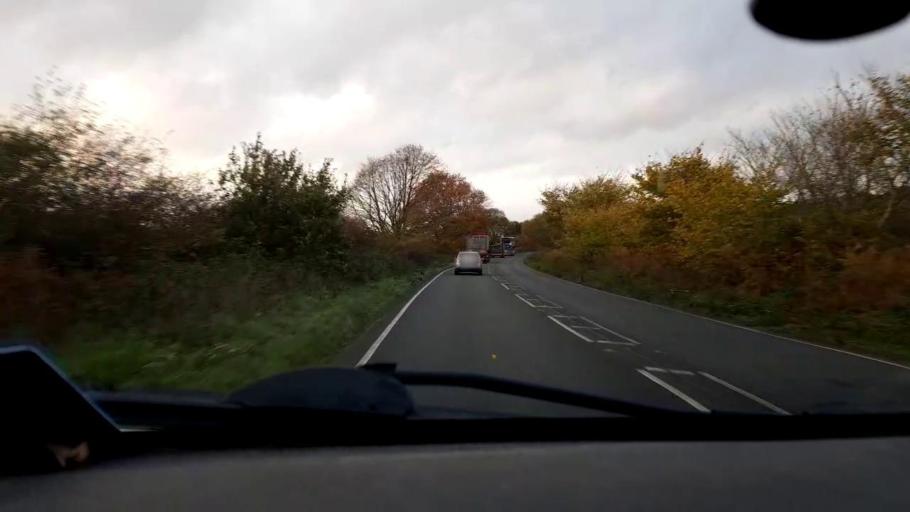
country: GB
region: England
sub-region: Norfolk
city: Costessey
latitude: 52.6987
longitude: 1.1628
